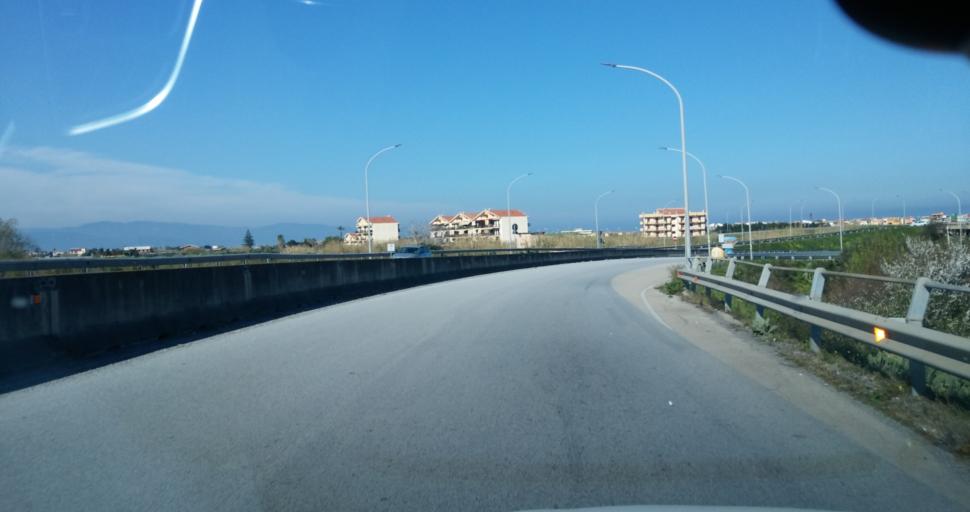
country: IT
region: Sicily
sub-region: Messina
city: Milazzo
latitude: 38.2061
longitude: 15.2403
